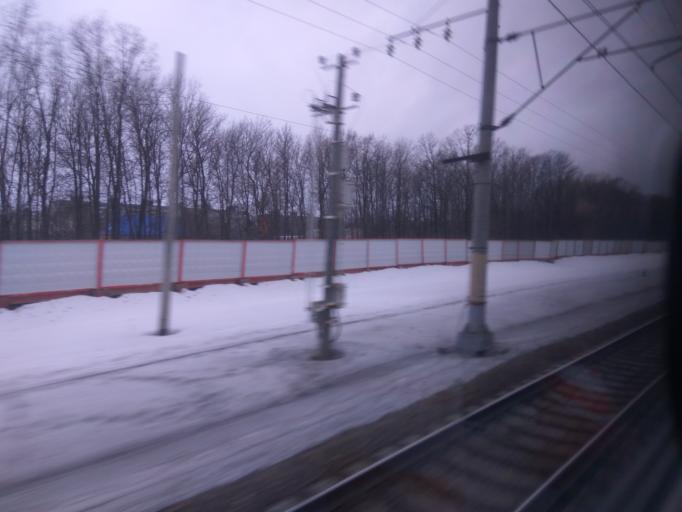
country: RU
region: Tverskaya
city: Tver
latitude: 56.8280
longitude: 35.9114
